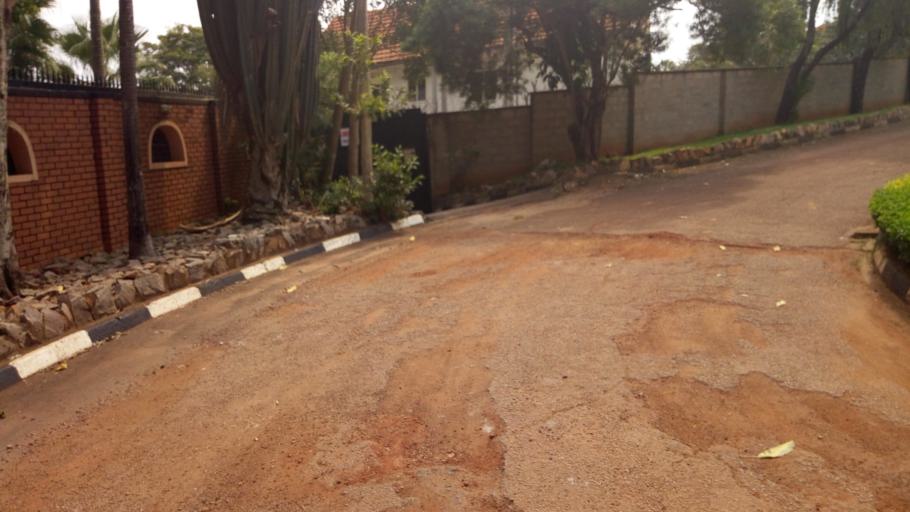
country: UG
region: Central Region
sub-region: Kampala District
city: Kampala
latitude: 0.3089
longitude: 32.6236
